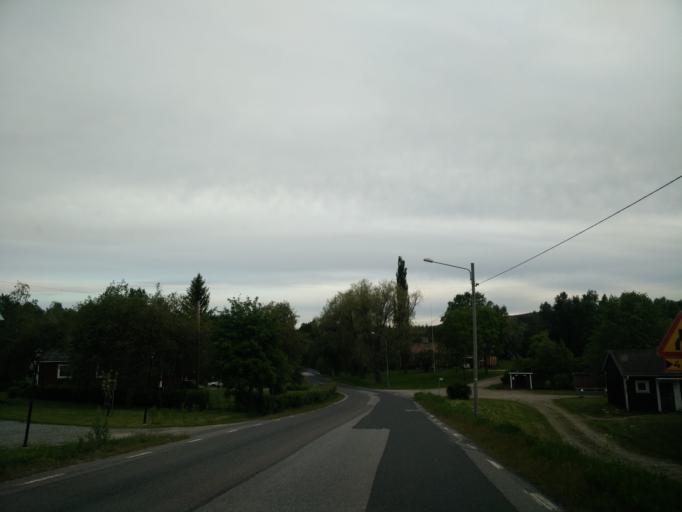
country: SE
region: Vaesternorrland
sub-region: Kramfors Kommun
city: Kramfors
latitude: 63.0488
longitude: 17.8017
